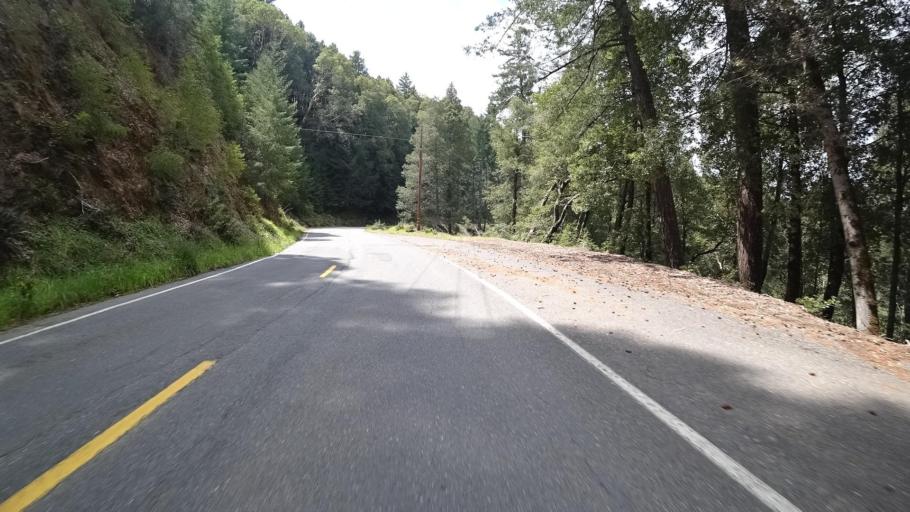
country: US
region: California
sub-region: Humboldt County
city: Redway
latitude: 40.0545
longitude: -123.9860
